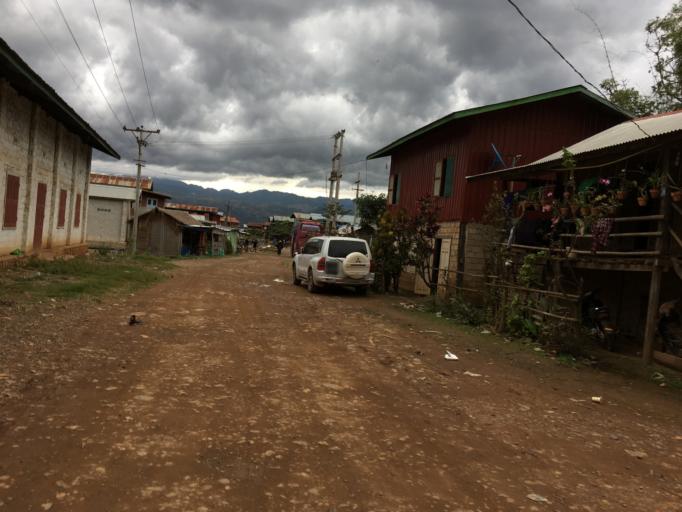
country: MM
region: Shan
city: Taunggyi
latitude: 20.6196
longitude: 96.8834
